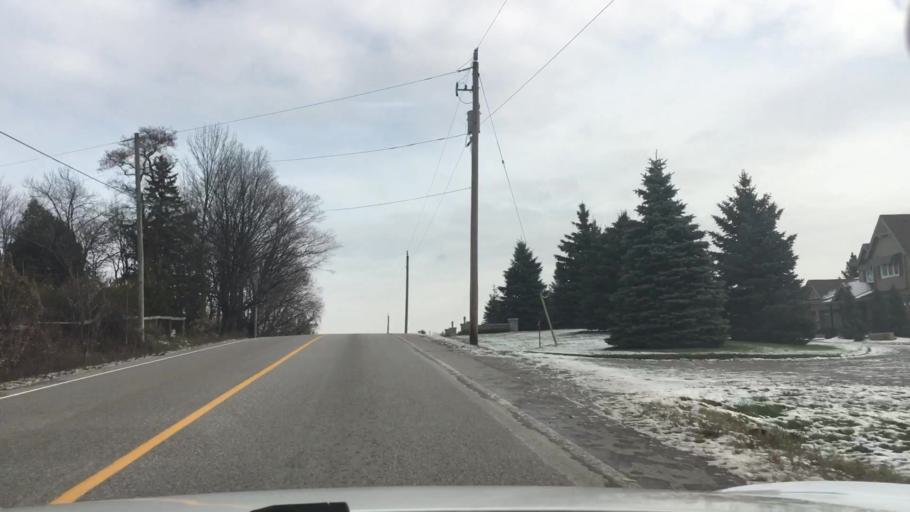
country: CA
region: Ontario
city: Oshawa
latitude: 43.9810
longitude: -78.8391
